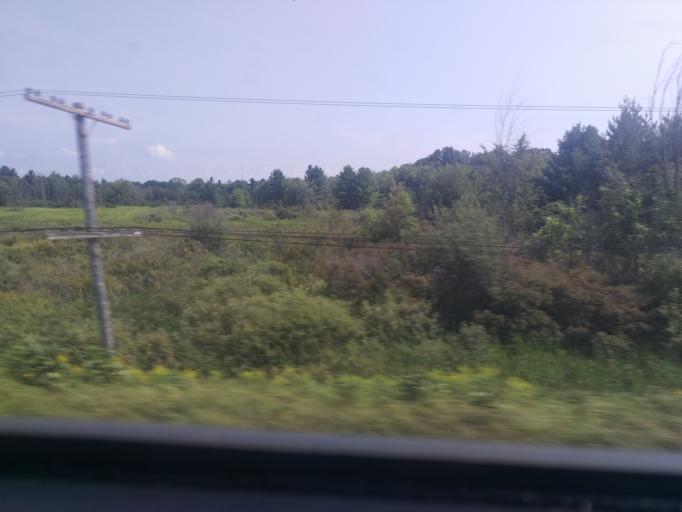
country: US
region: New York
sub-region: Jefferson County
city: Alexandria Bay
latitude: 44.4593
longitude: -75.9160
